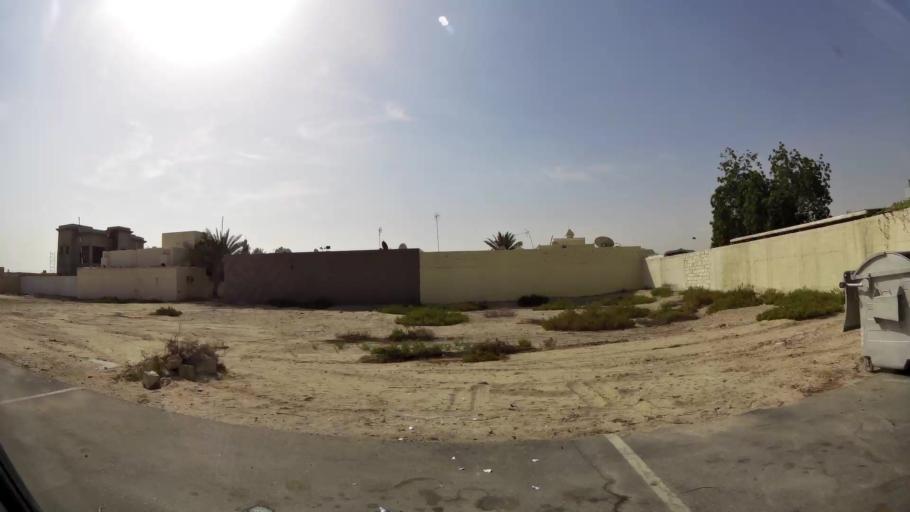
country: AE
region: Ash Shariqah
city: Sharjah
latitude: 25.2605
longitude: 55.3934
